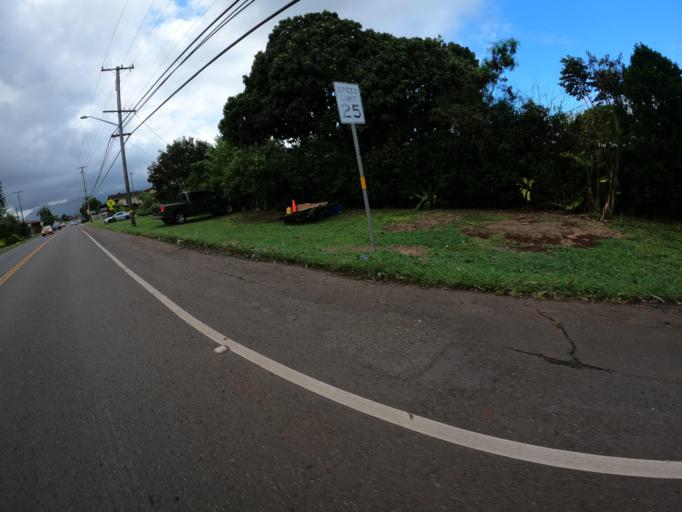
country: US
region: Hawaii
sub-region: Honolulu County
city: Whitmore Village
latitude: 21.5108
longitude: -158.0210
